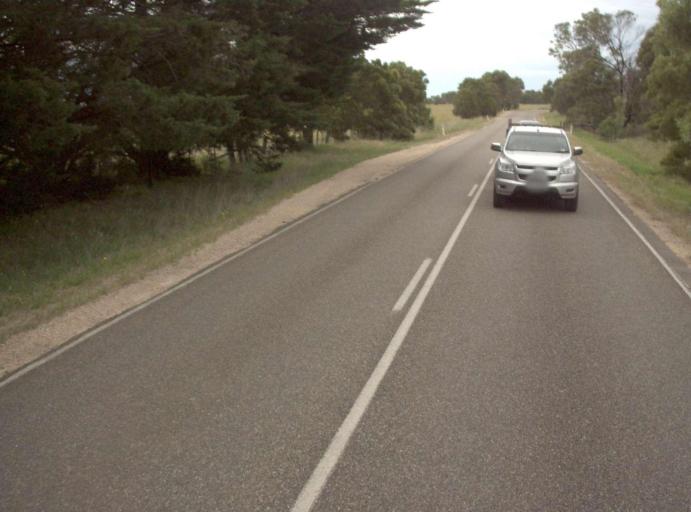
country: AU
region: Victoria
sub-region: East Gippsland
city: Bairnsdale
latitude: -37.8208
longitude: 147.5020
